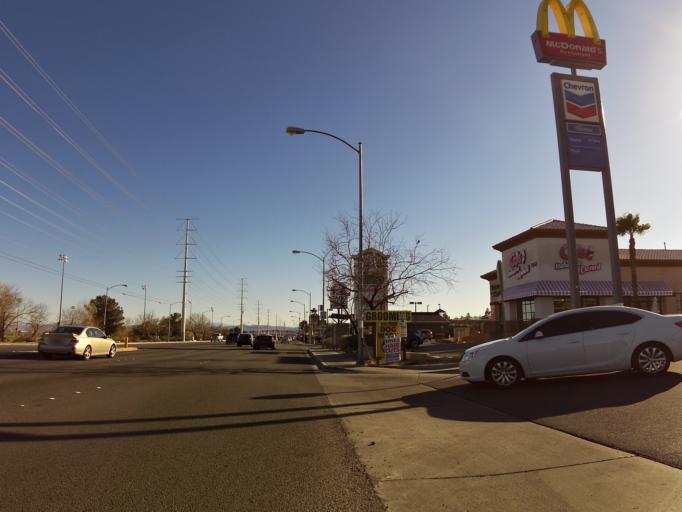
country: US
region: Nevada
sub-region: Clark County
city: Spring Valley
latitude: 36.1255
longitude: -115.2792
